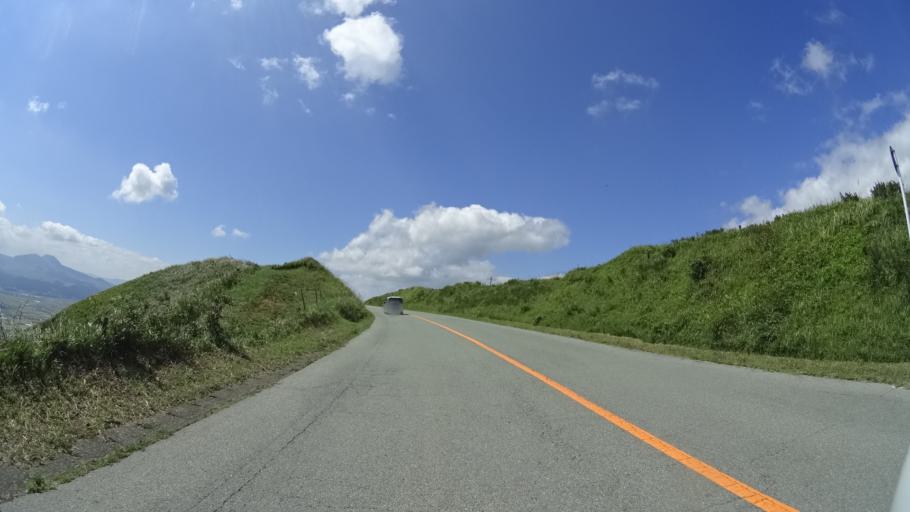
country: JP
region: Kumamoto
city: Aso
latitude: 32.9999
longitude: 131.0873
